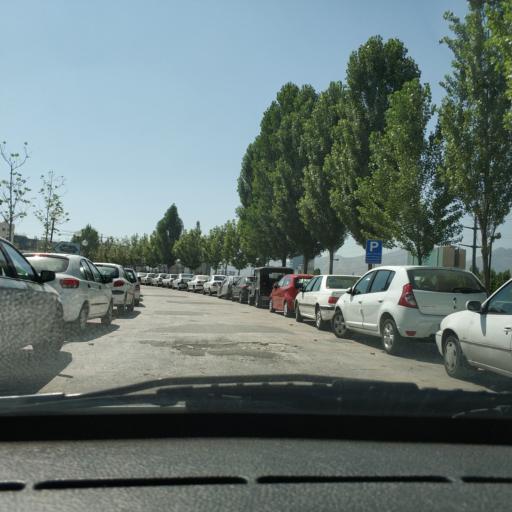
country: IR
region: Tehran
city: Tajrish
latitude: 35.7567
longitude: 51.4335
